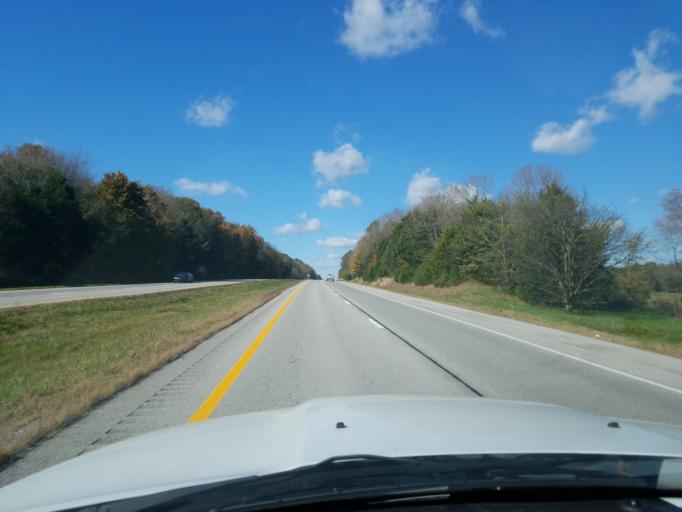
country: US
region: Kentucky
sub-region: Barren County
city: Glasgow
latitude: 36.9964
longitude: -85.8262
